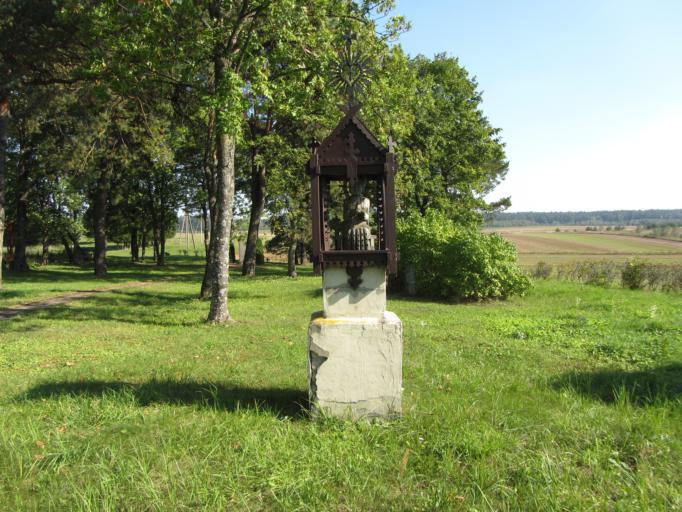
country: LT
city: Aukstadvaris
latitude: 54.4811
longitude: 24.5969
